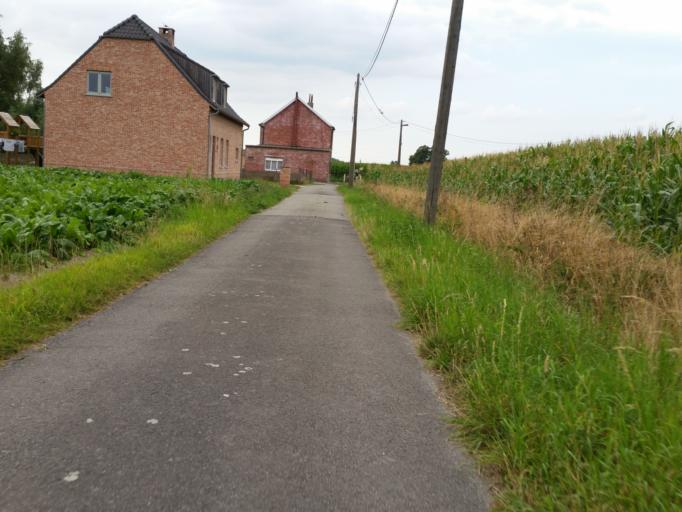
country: BE
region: Flanders
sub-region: Provincie Antwerpen
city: Rumst
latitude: 51.0976
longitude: 4.4400
